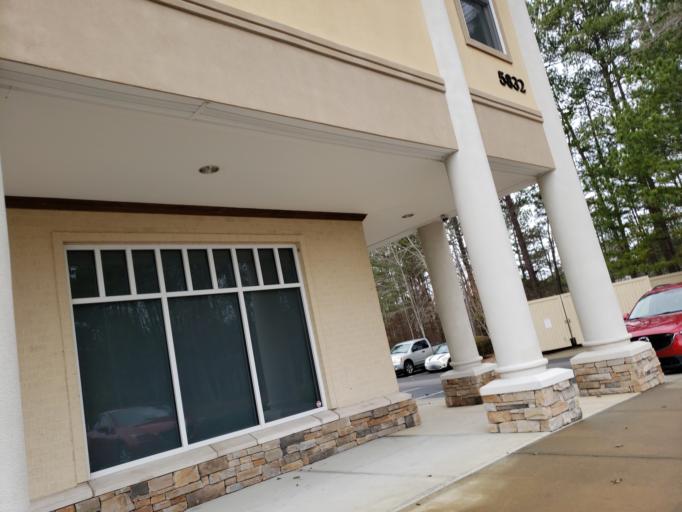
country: US
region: North Carolina
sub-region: Durham County
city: Durham
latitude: 35.9211
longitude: -78.9305
